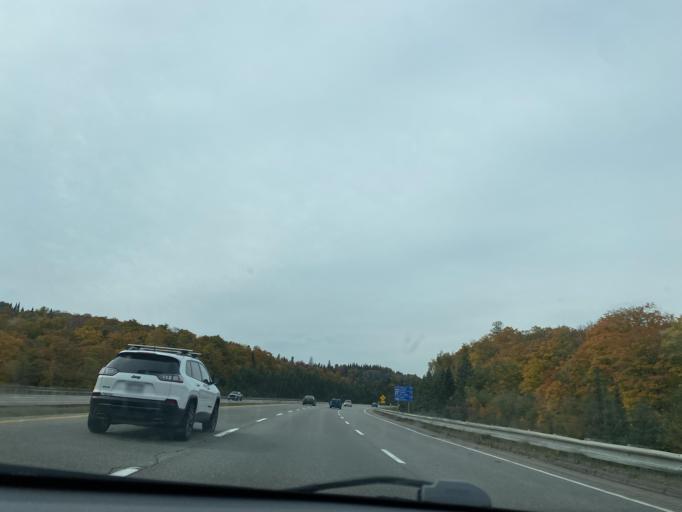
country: CA
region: Quebec
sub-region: Laurentides
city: Val-David
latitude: 46.0245
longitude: -74.2459
